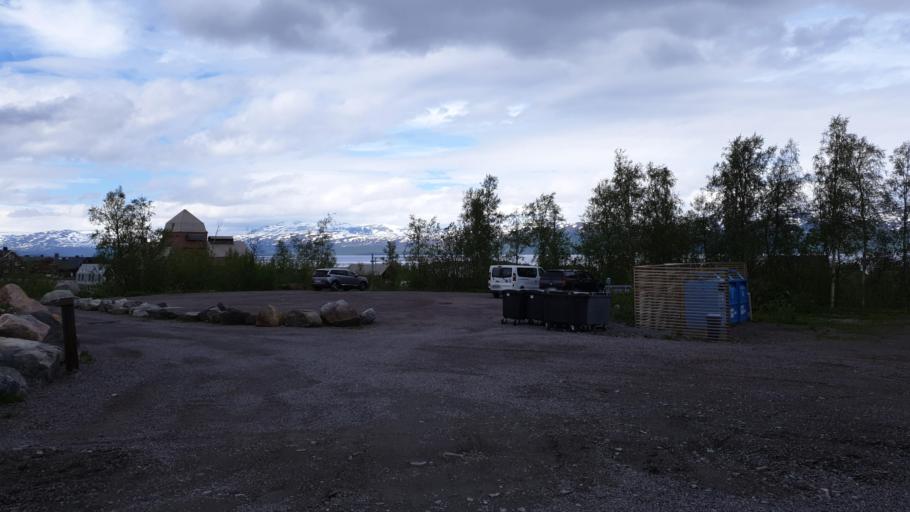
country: NO
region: Troms
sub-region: Bardu
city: Setermoen
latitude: 68.3469
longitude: 18.8320
